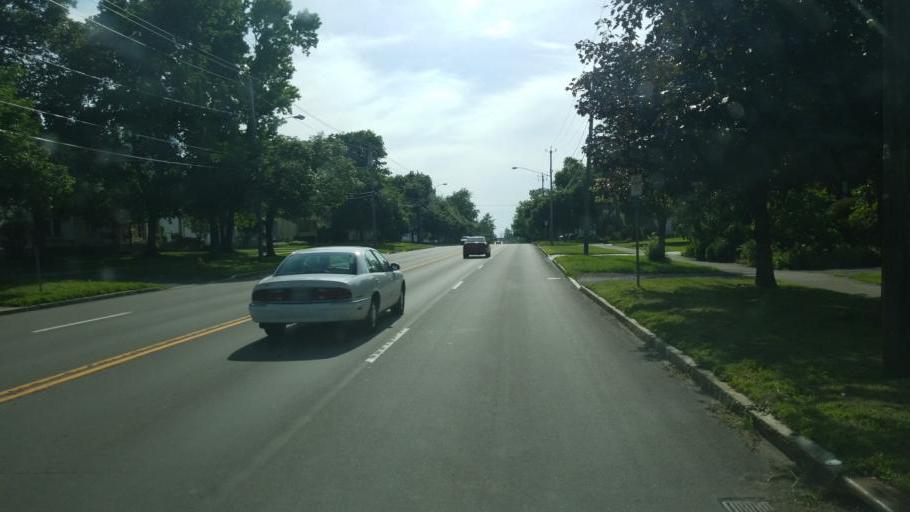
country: US
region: New York
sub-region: Genesee County
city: Le Roy
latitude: 42.9778
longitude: -77.9942
